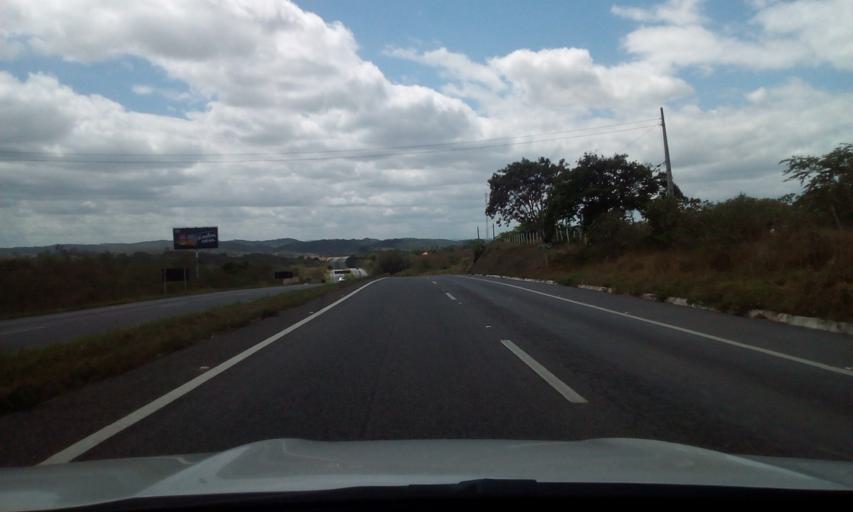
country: BR
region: Paraiba
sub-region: Campina Grande
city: Campina Grande
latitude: -7.2548
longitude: -35.8280
